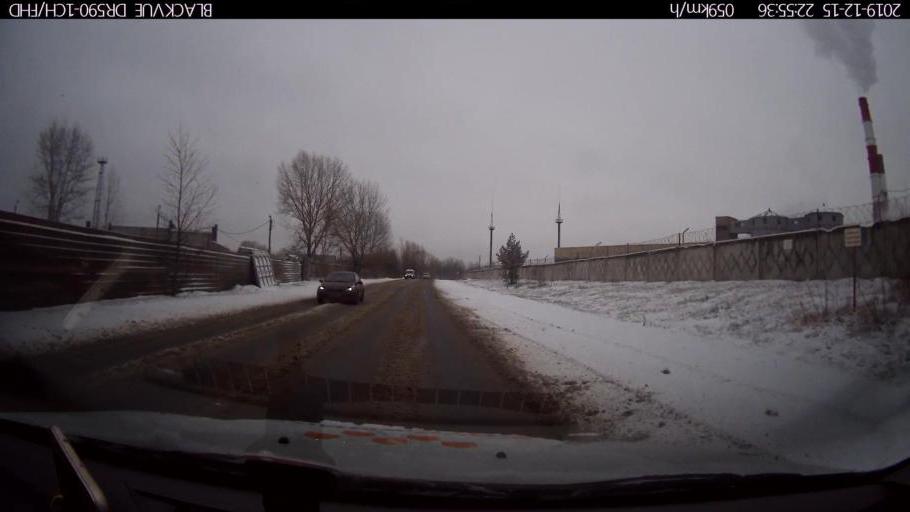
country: RU
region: Nizjnij Novgorod
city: Neklyudovo
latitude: 56.3562
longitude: 43.8928
